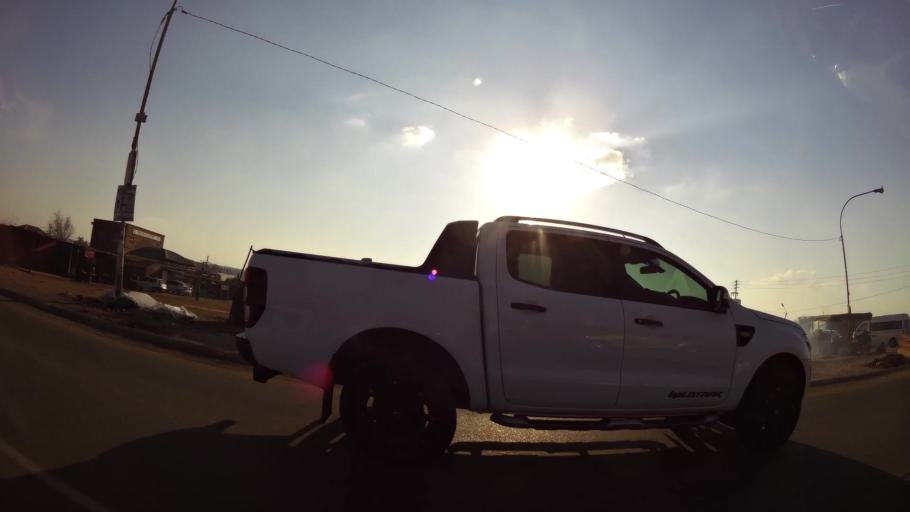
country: ZA
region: Gauteng
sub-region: Ekurhuleni Metropolitan Municipality
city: Tembisa
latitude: -25.9710
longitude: 28.2136
